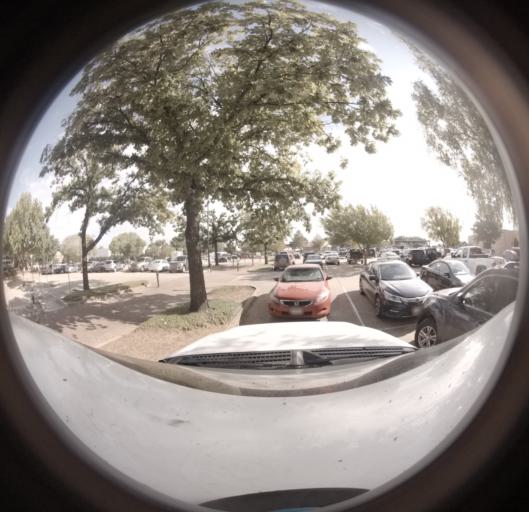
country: US
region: Texas
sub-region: Ector County
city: West Odessa
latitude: 31.7421
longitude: -102.5323
